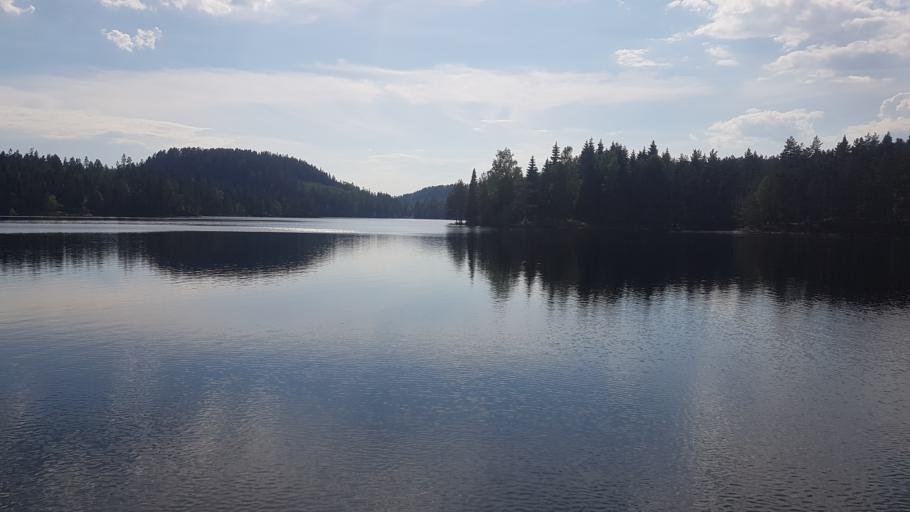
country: NO
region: Akershus
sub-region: Raelingen
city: Fjerdingby
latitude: 59.8892
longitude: 11.0656
